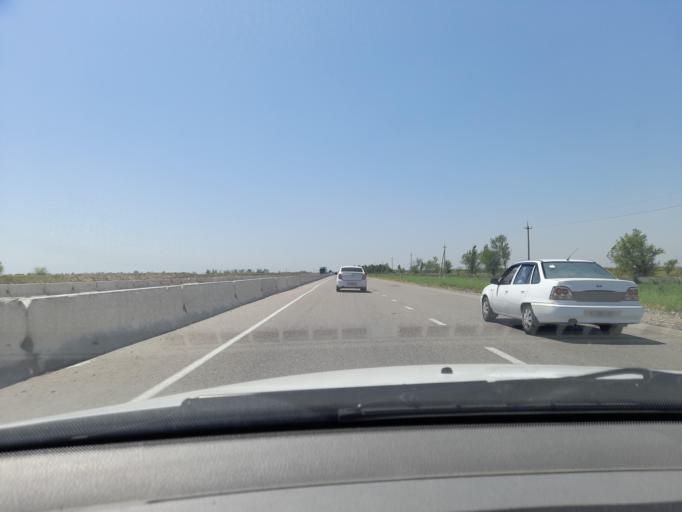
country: UZ
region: Jizzax
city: Dustlik
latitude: 40.4346
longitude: 68.2301
